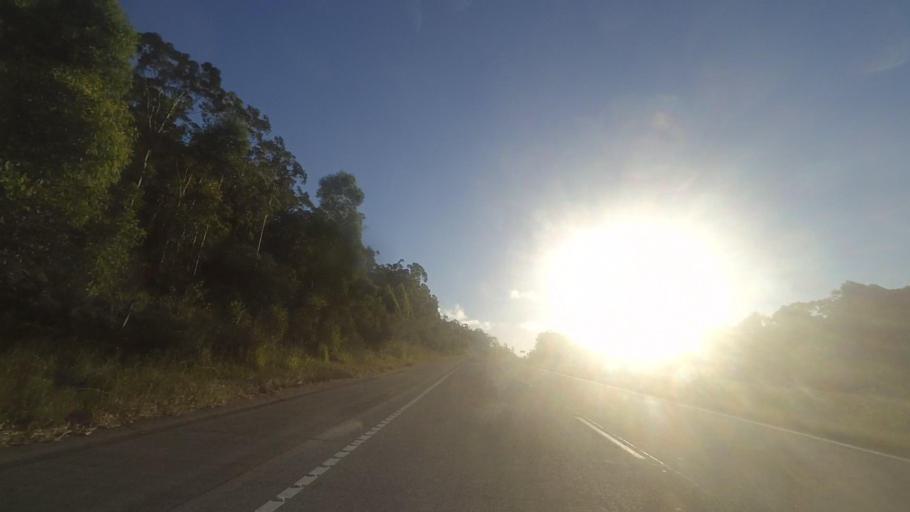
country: AU
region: New South Wales
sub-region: Great Lakes
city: Bulahdelah
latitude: -32.5329
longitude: 152.1820
